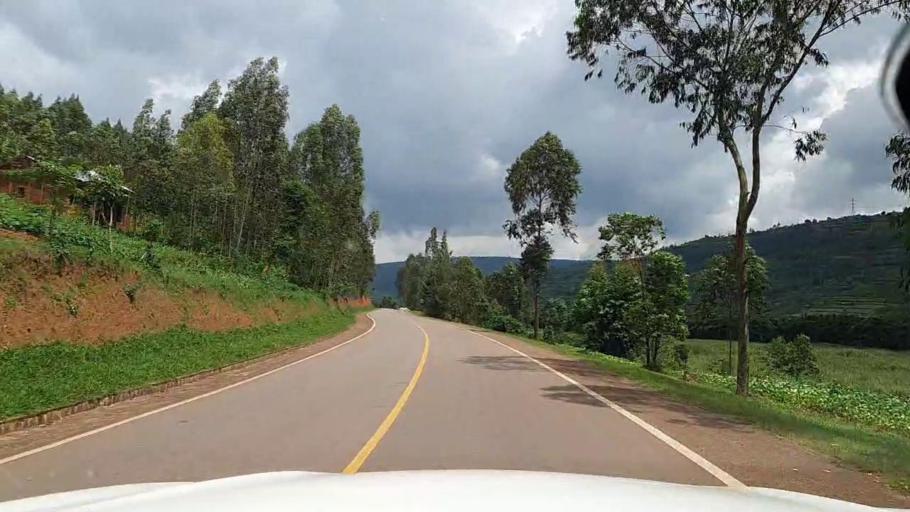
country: RW
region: Kigali
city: Kigali
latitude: -1.8022
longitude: 30.1283
